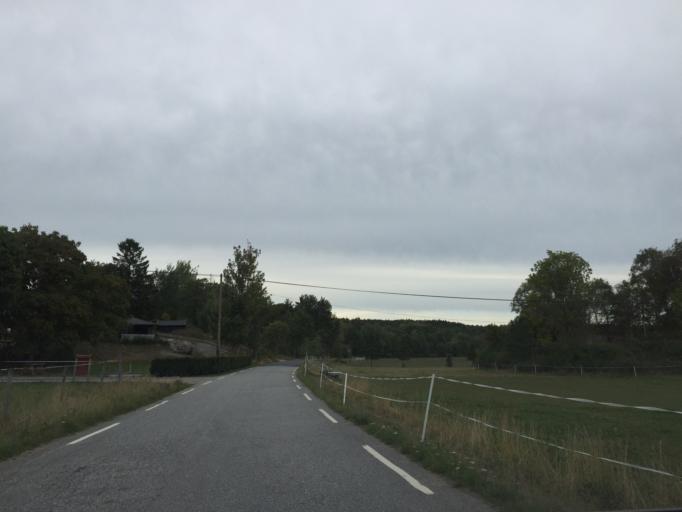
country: NO
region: Ostfold
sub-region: Hvaler
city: Skjaerhalden
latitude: 59.0639
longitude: 11.0330
